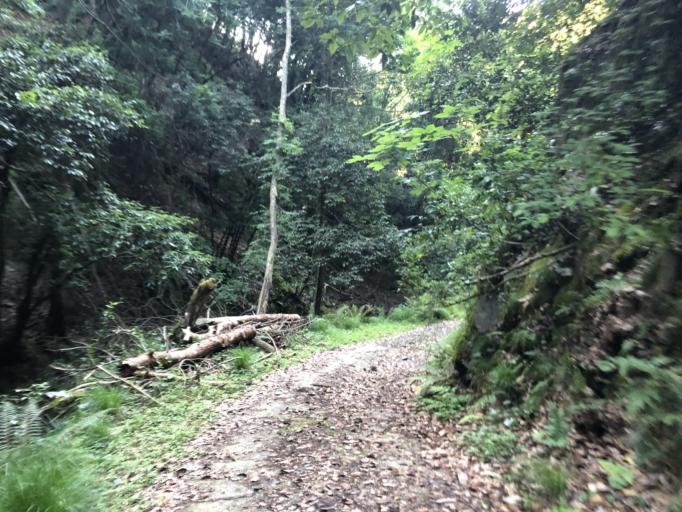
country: JP
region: Kyoto
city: Kameoka
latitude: 34.9869
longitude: 135.6232
